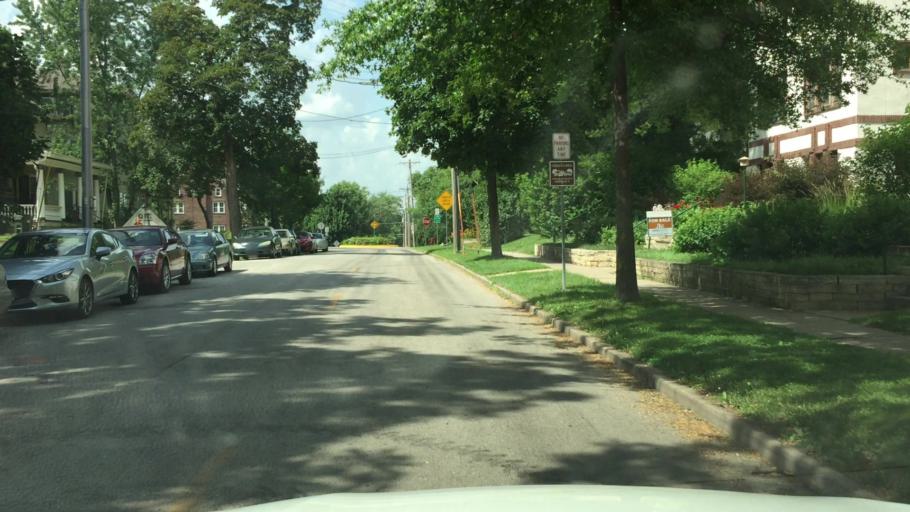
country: US
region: Iowa
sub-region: Johnson County
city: Iowa City
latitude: 41.6580
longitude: -91.5212
